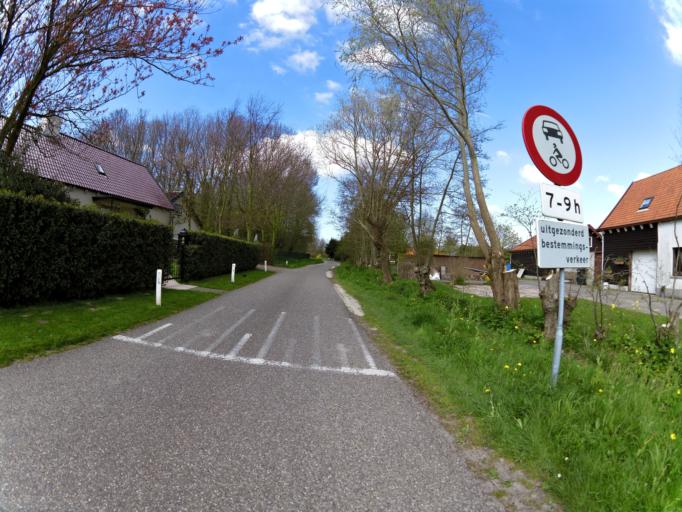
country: NL
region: South Holland
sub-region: Gemeente Brielle
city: Brielle
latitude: 51.9061
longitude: 4.1124
